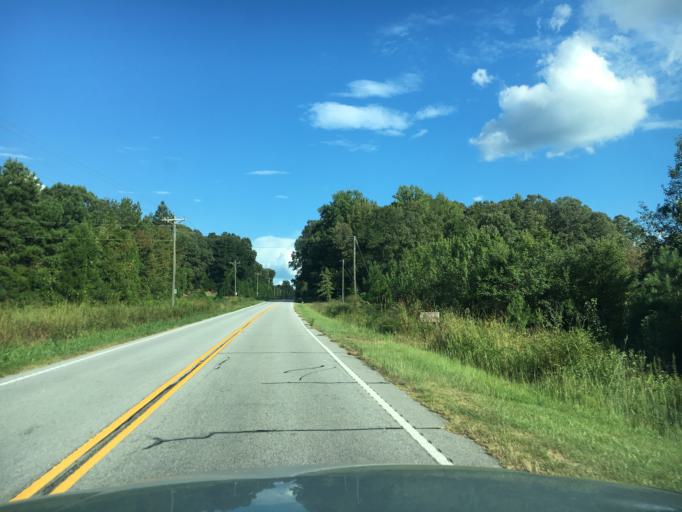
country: US
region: South Carolina
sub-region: Laurens County
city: Laurens
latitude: 34.5255
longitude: -82.1241
